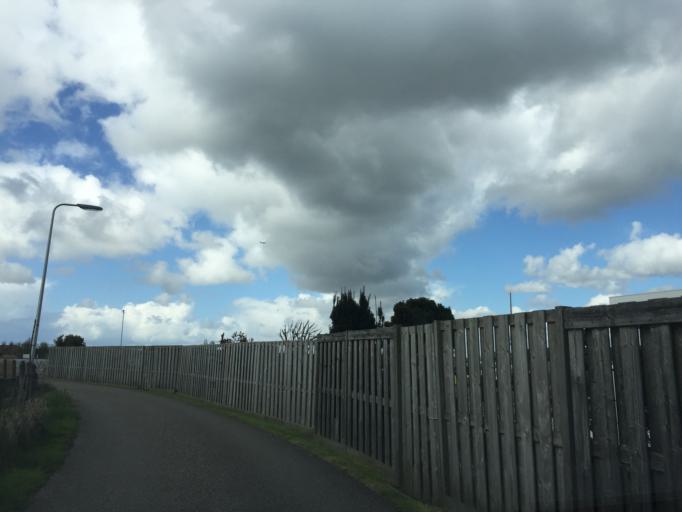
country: NL
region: South Holland
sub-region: Gemeente Kaag en Braassem
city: Oude Wetering
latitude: 52.1959
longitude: 4.5828
